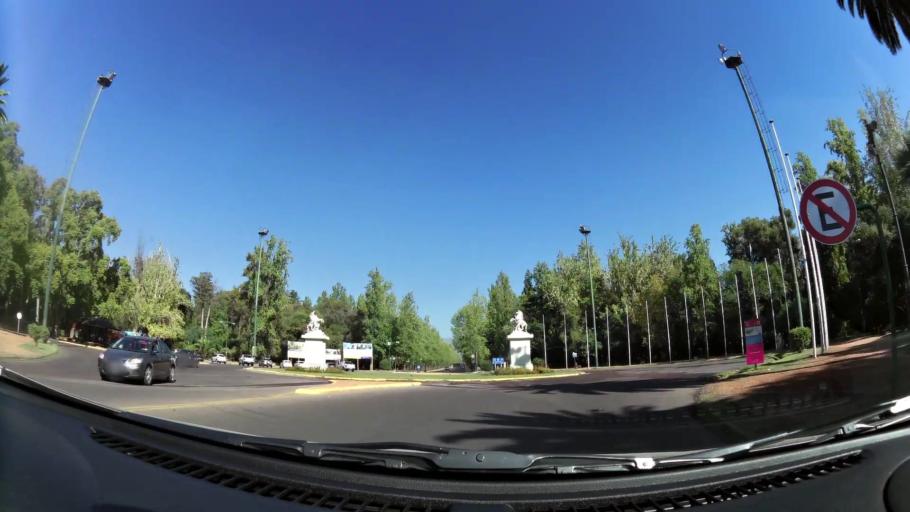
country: AR
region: Mendoza
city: Mendoza
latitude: -32.8863
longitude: -68.8625
